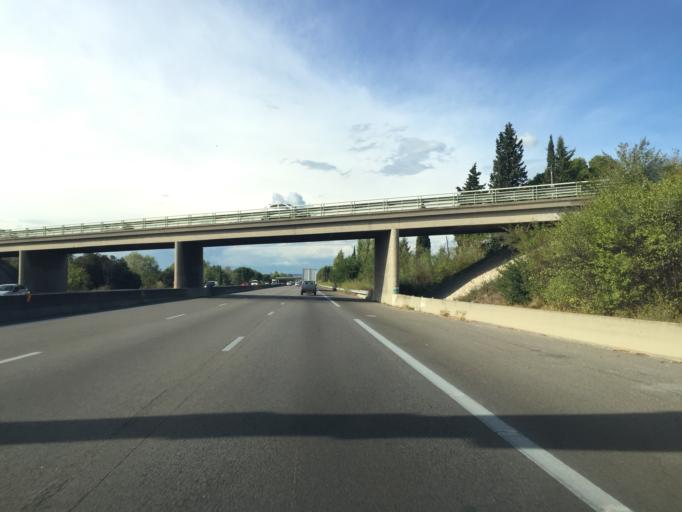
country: FR
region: Provence-Alpes-Cote d'Azur
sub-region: Departement du Vaucluse
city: Morieres-les-Avignon
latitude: 43.9534
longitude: 4.9072
